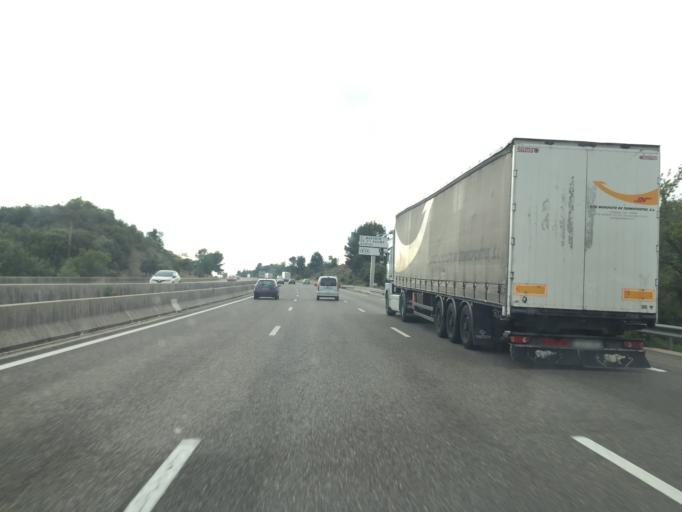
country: FR
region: Provence-Alpes-Cote d'Azur
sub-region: Departement du Var
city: Saint-Maximin-la-Sainte-Baume
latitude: 43.4445
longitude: 5.9001
